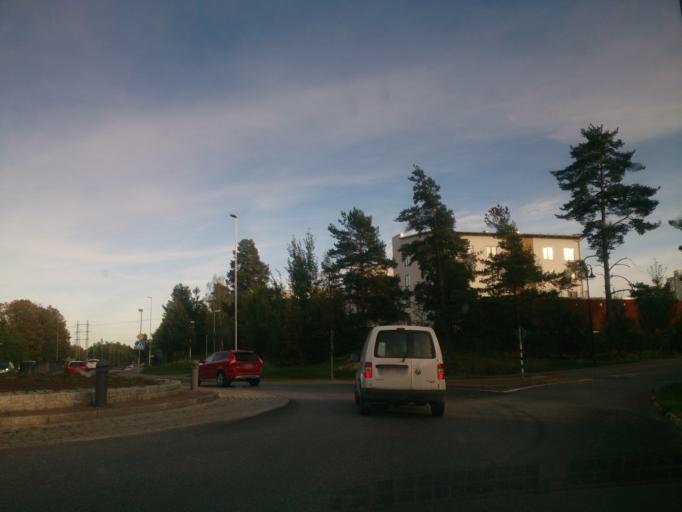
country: SE
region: Stockholm
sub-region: Tyreso Kommun
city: Bollmora
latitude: 59.2496
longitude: 18.2347
